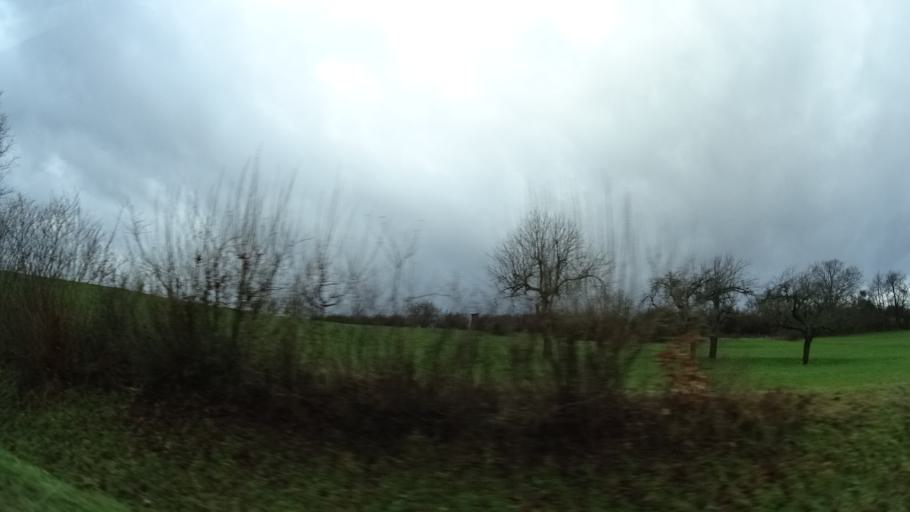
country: DE
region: Hesse
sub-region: Regierungsbezirk Darmstadt
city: Steinau an der Strasse
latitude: 50.3220
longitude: 9.4775
